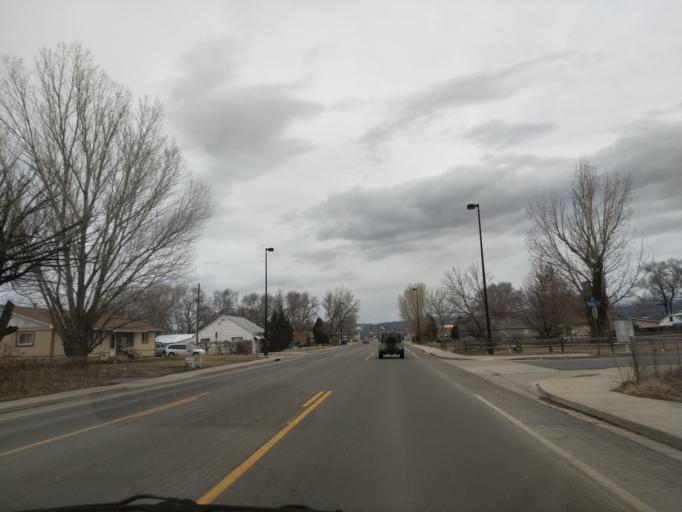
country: US
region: Colorado
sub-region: Mesa County
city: Fruitvale
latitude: 39.0798
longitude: -108.5152
